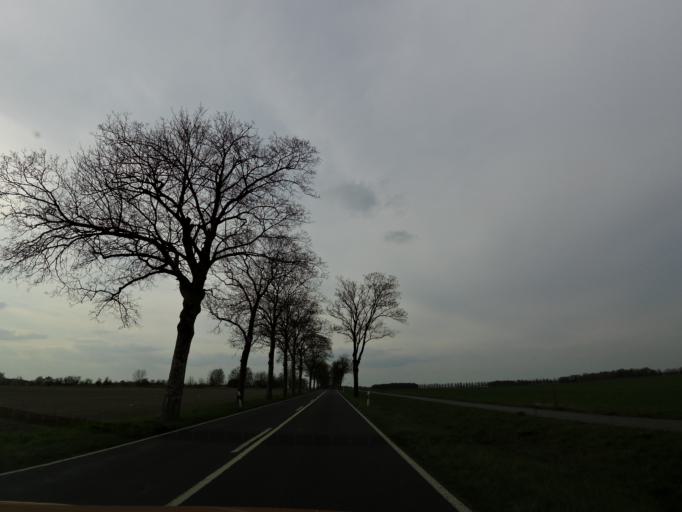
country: DE
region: Brandenburg
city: Mittenwalde
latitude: 52.2915
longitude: 13.5219
